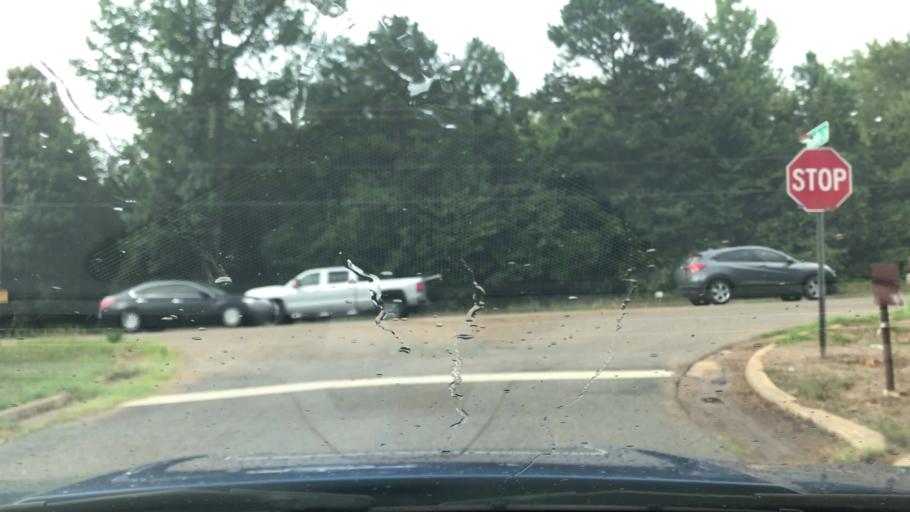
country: US
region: Louisiana
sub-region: Caddo Parish
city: Greenwood
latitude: 32.4479
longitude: -94.0098
